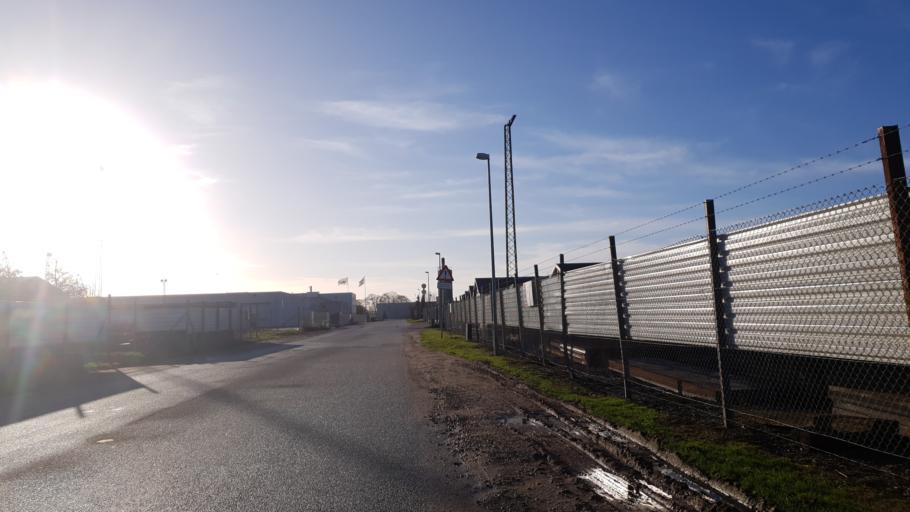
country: DK
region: Central Jutland
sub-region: Hedensted Kommune
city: Hedensted
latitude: 55.7955
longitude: 9.6739
